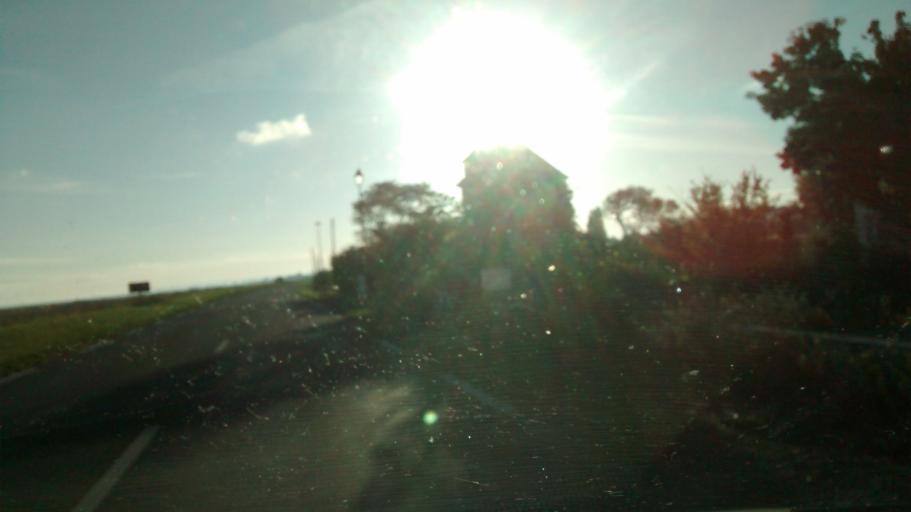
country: FR
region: Brittany
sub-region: Departement d'Ille-et-Vilaine
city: La Fresnais
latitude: 48.6131
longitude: -1.8373
